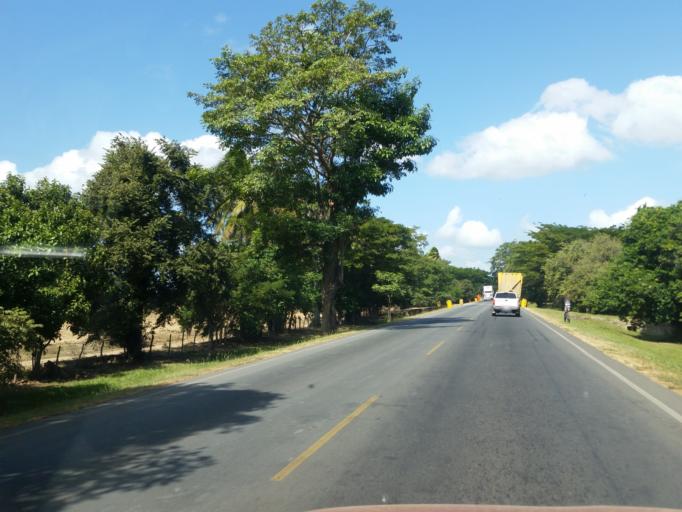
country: NI
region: Granada
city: Nandaime
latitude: 11.7418
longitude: -86.0231
